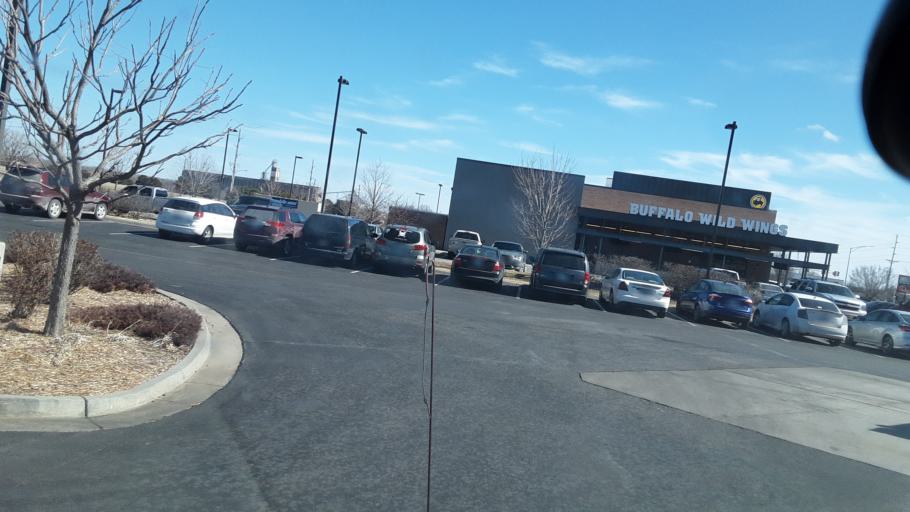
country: US
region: Kansas
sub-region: Reno County
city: Hutchinson
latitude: 38.0729
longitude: -97.8971
